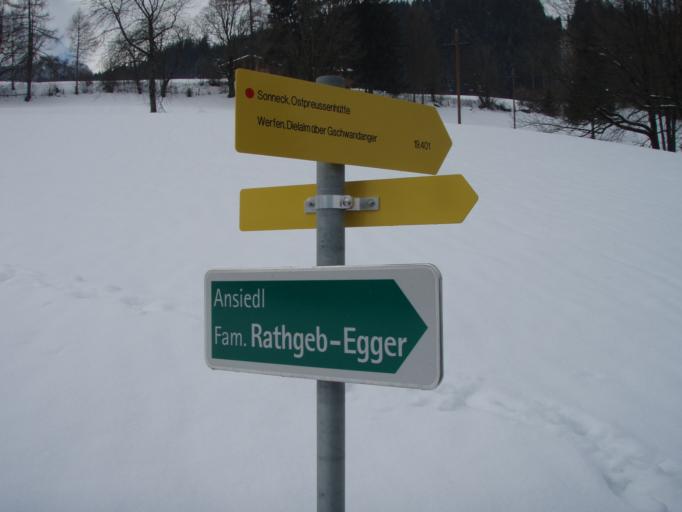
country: AT
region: Salzburg
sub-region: Politischer Bezirk Sankt Johann im Pongau
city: Werfen
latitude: 47.4637
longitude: 13.1870
